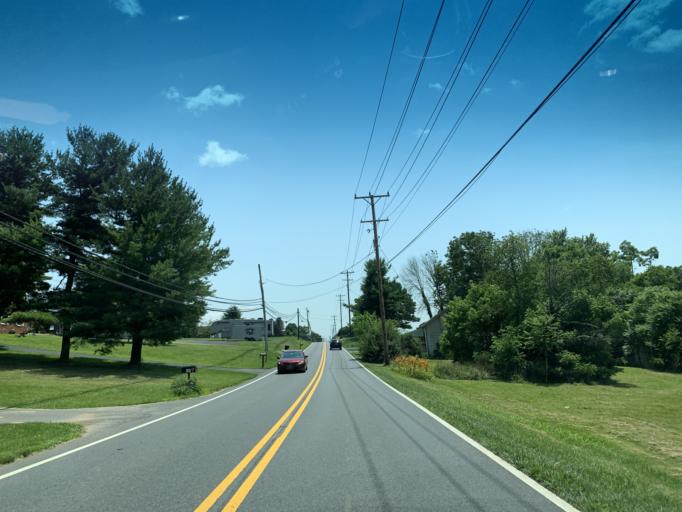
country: US
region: Maryland
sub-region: Frederick County
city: Green Valley
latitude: 39.3599
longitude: -77.2695
